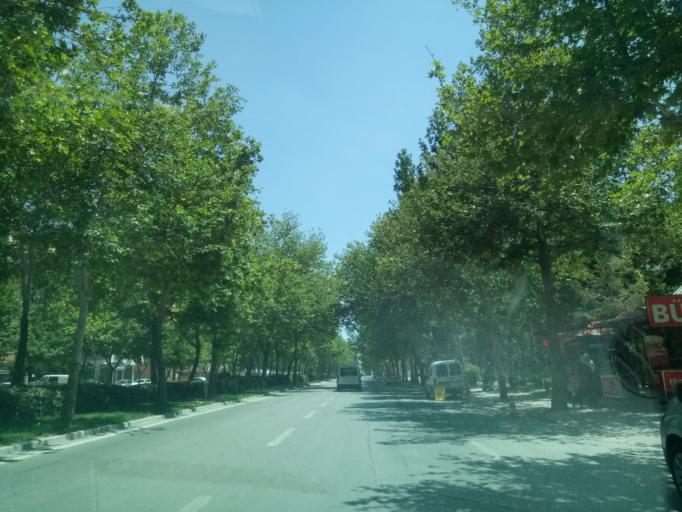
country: TR
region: Konya
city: Konya
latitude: 37.8487
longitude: 32.5009
